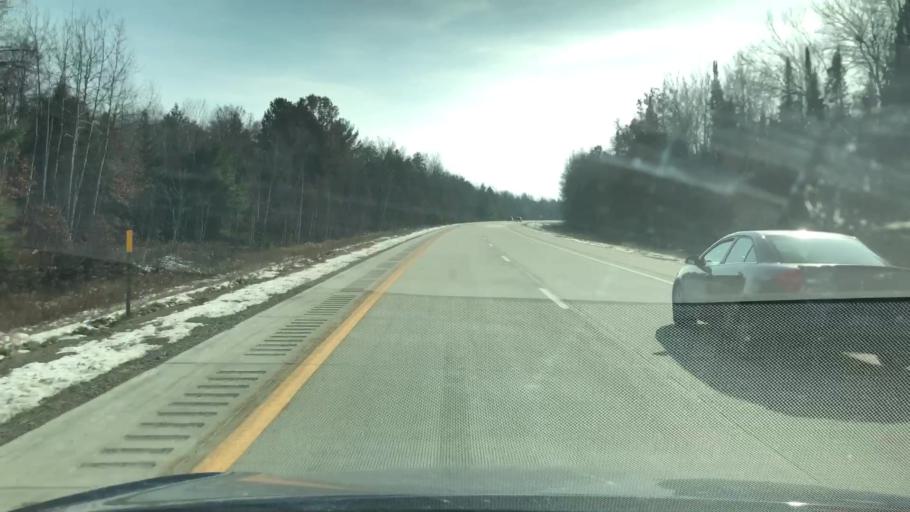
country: US
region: Michigan
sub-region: Ogemaw County
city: West Branch
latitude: 44.2034
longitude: -84.1908
